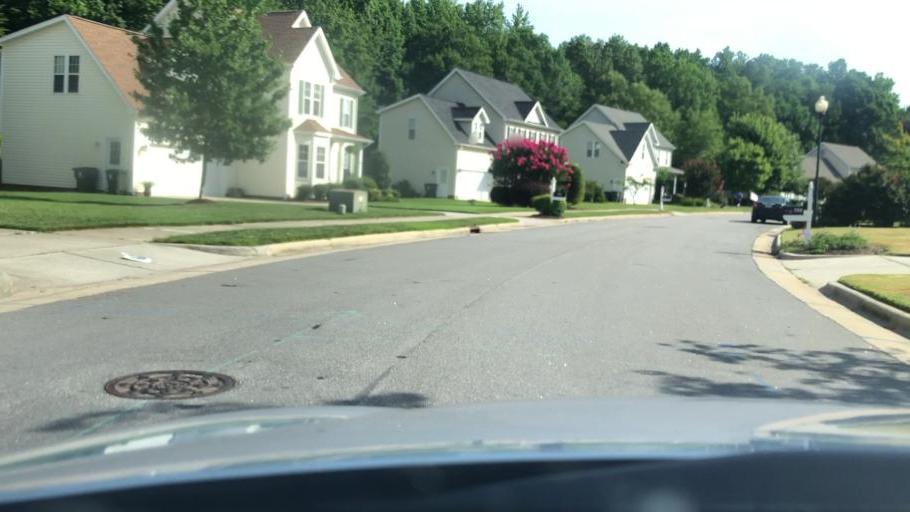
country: US
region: North Carolina
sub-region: Wake County
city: Apex
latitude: 35.7327
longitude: -78.8869
